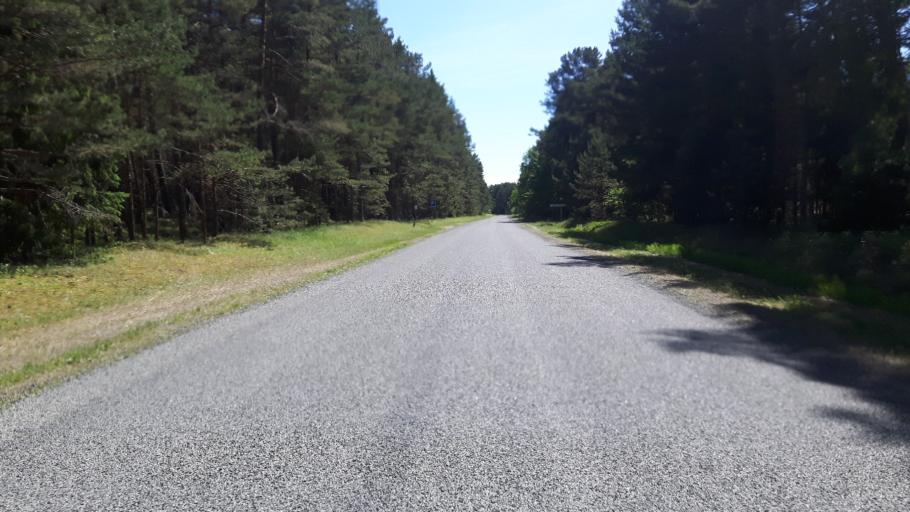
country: LV
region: Salacgrivas
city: Ainazi
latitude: 57.9393
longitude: 24.3922
